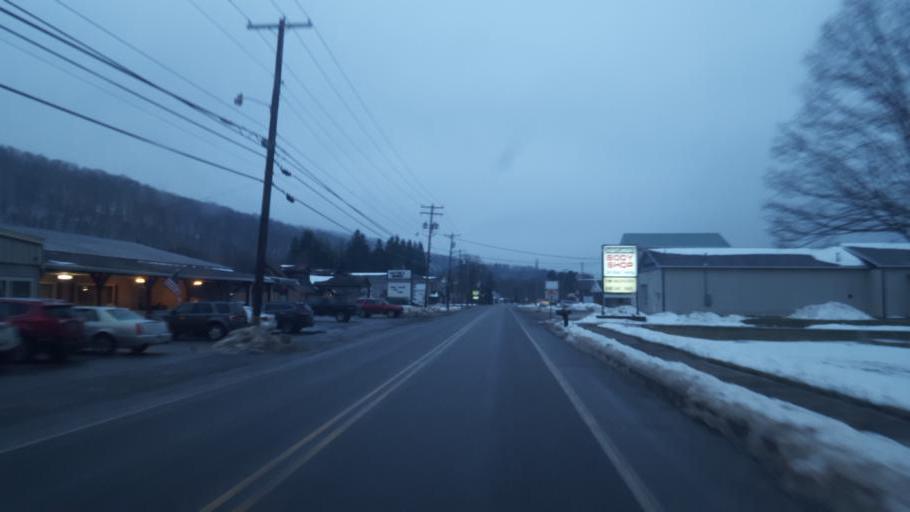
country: US
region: Pennsylvania
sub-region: Potter County
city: Coudersport
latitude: 41.7659
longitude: -78.0317
